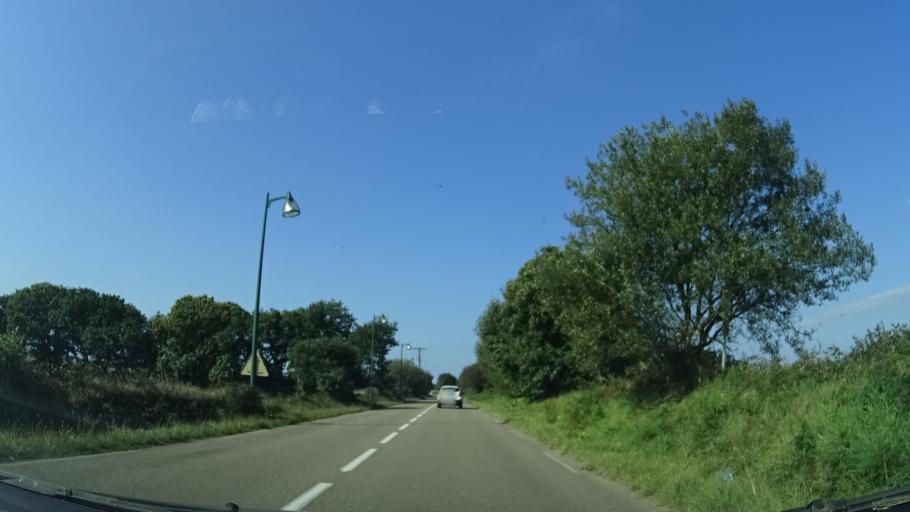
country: FR
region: Brittany
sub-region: Departement du Finistere
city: Douarnenez
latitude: 48.0919
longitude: -4.2757
